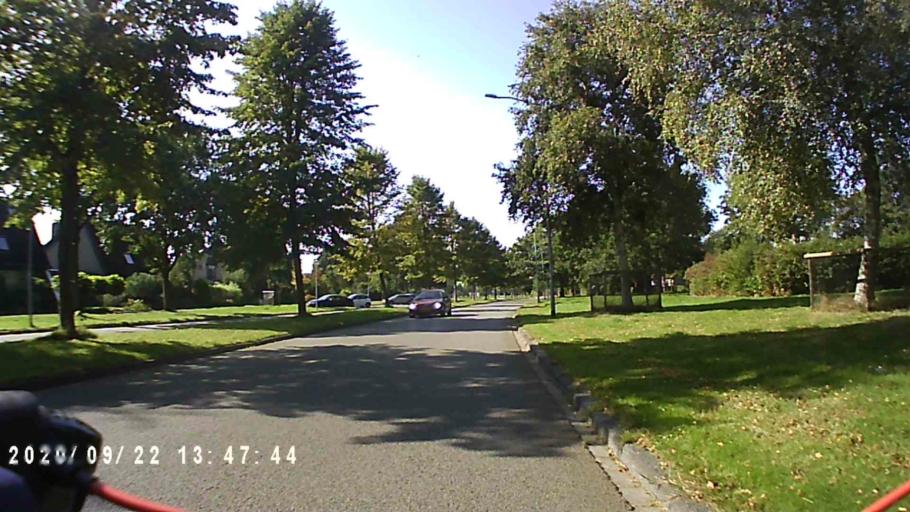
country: NL
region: Groningen
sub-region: Gemeente Leek
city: Leek
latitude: 53.1408
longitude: 6.4091
